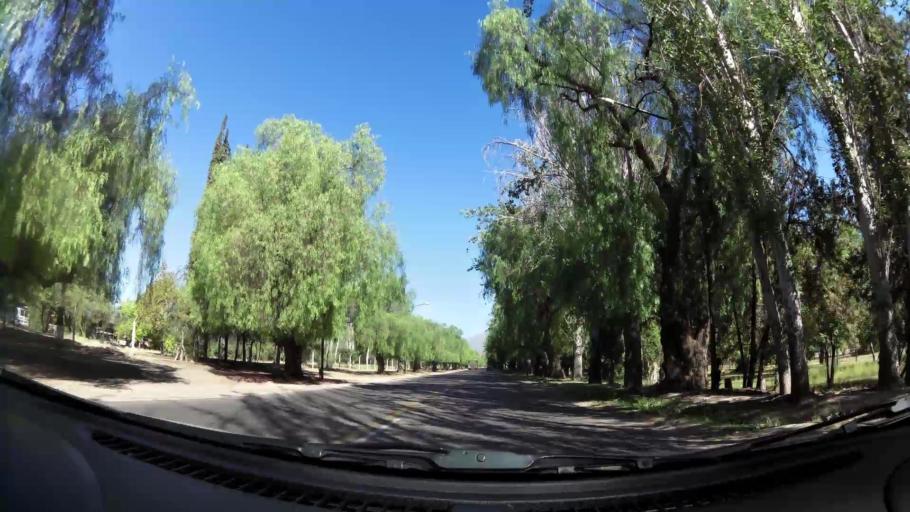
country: AR
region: Mendoza
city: Mendoza
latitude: -32.8929
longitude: -68.8754
